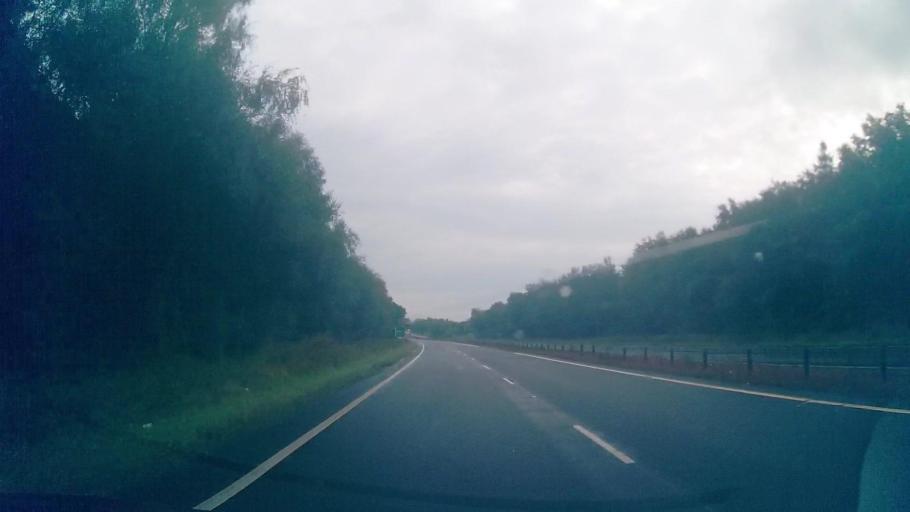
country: GB
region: Scotland
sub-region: Dumfries and Galloway
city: Locharbriggs
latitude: 55.0675
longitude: -3.5291
